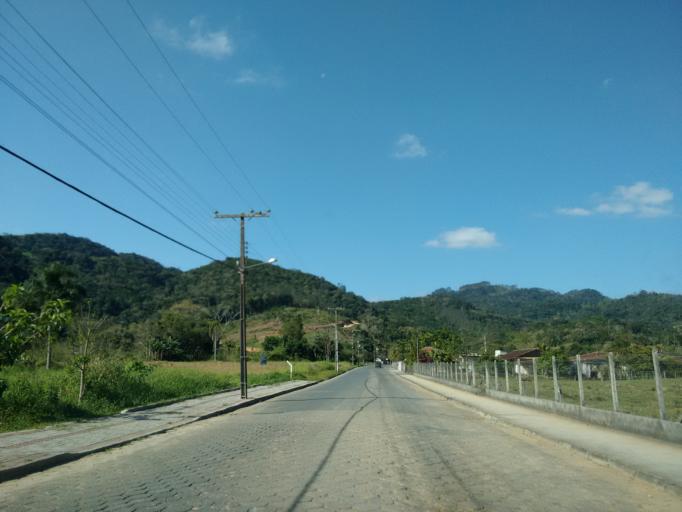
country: BR
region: Santa Catarina
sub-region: Pomerode
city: Pomerode
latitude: -26.7387
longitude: -49.1679
